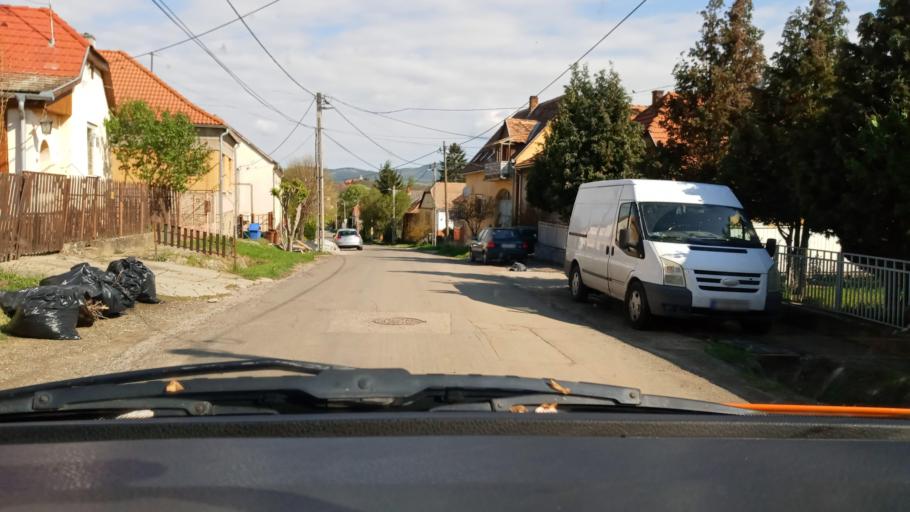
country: HU
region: Baranya
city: Hosszuheteny
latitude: 46.1057
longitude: 18.3443
